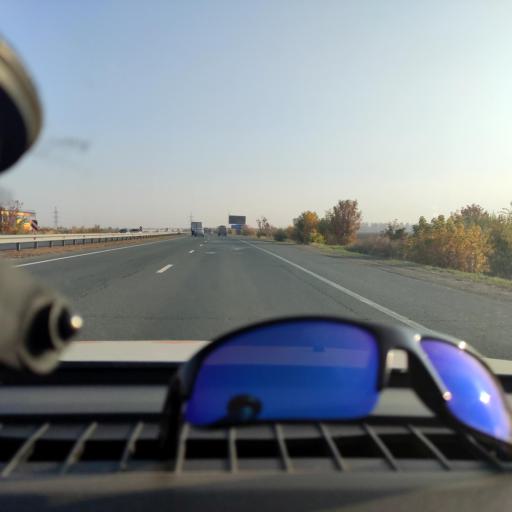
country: RU
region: Samara
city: Novokuybyshevsk
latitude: 53.0046
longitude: 49.9695
